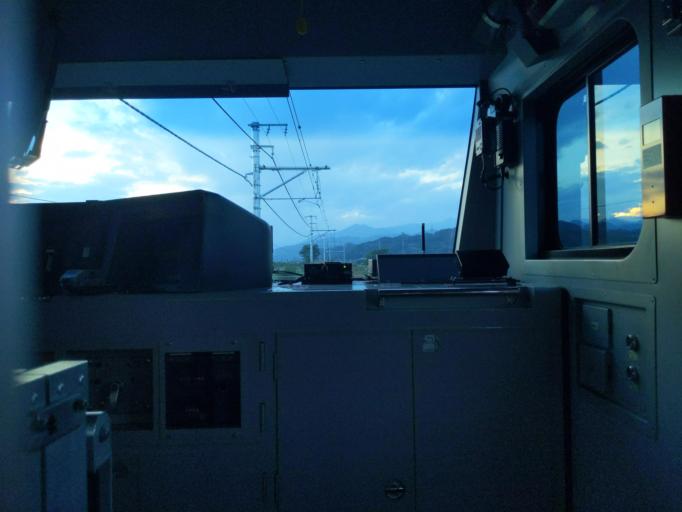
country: JP
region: Tokyo
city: Itsukaichi
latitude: 35.7303
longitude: 139.2645
